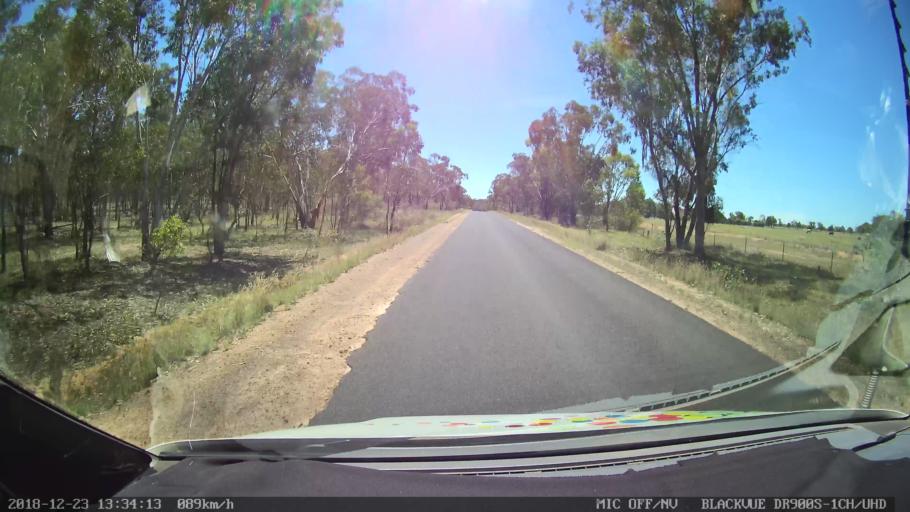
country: AU
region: New South Wales
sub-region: Armidale Dumaresq
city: Armidale
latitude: -30.4518
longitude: 151.2672
